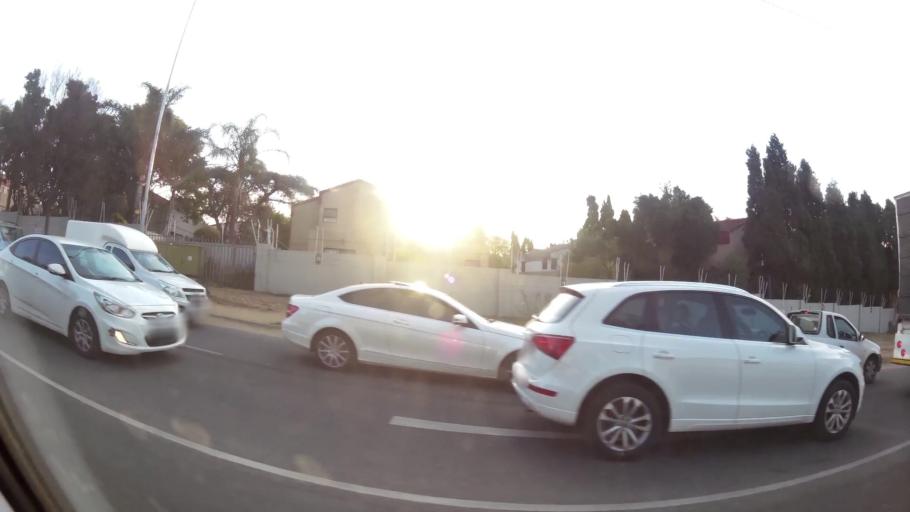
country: ZA
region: Gauteng
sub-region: City of Johannesburg Metropolitan Municipality
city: Diepsloot
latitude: -26.0106
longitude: 28.0003
